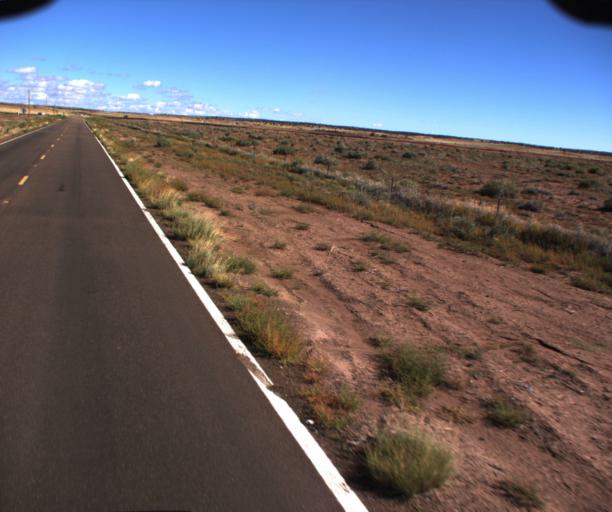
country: US
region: Arizona
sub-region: Apache County
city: Saint Johns
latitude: 34.6271
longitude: -109.3131
